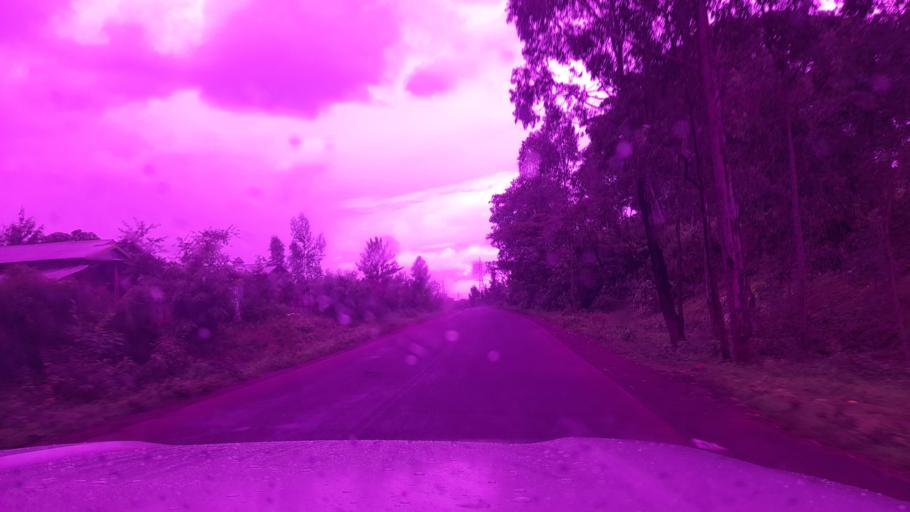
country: ET
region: Oromiya
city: Jima
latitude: 7.7085
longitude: 37.0589
